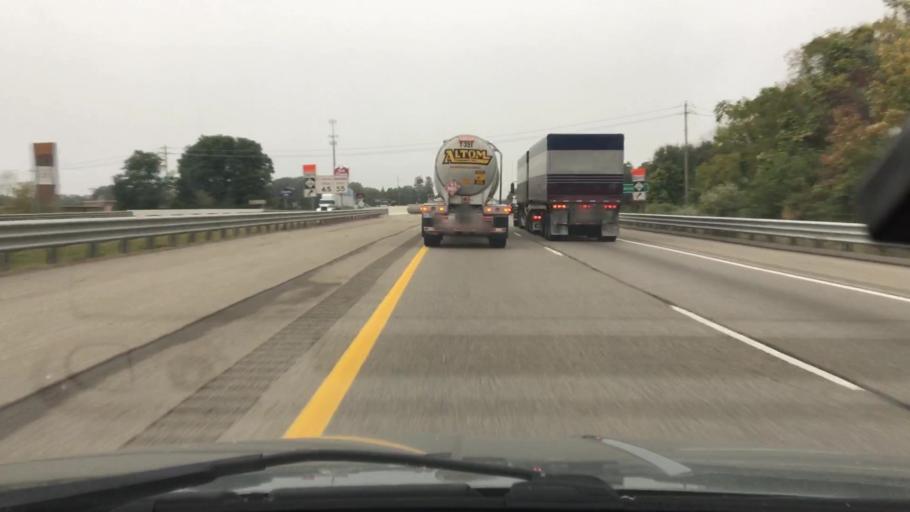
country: US
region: Michigan
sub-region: Calhoun County
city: Lakeview
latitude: 42.2636
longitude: -85.1877
